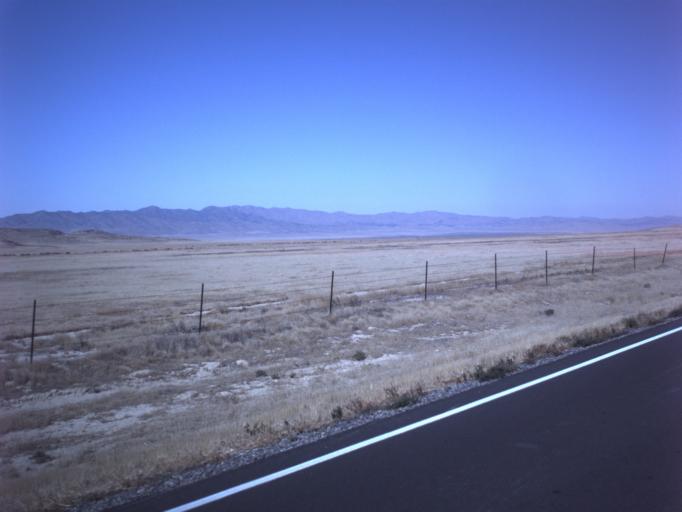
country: US
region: Utah
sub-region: Tooele County
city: Grantsville
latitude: 40.3759
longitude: -112.7466
